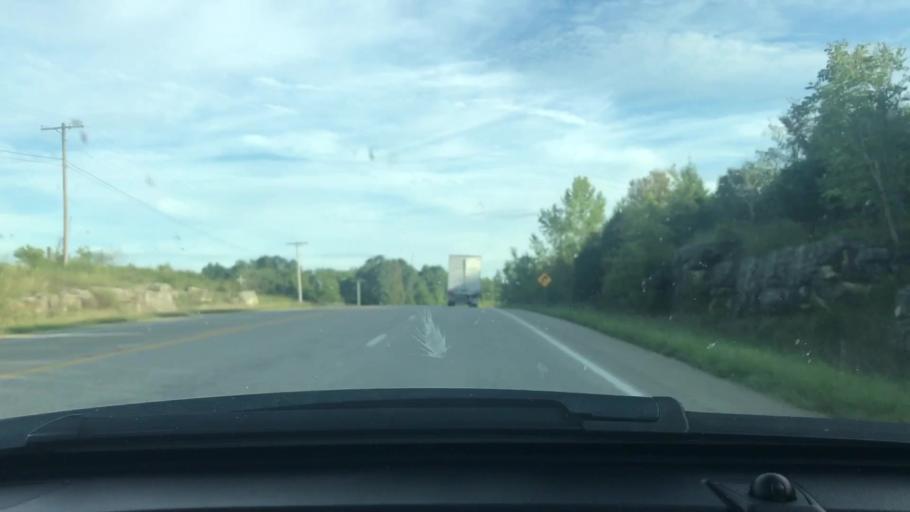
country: US
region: Arkansas
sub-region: Randolph County
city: Pocahontas
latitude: 36.1900
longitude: -91.1642
